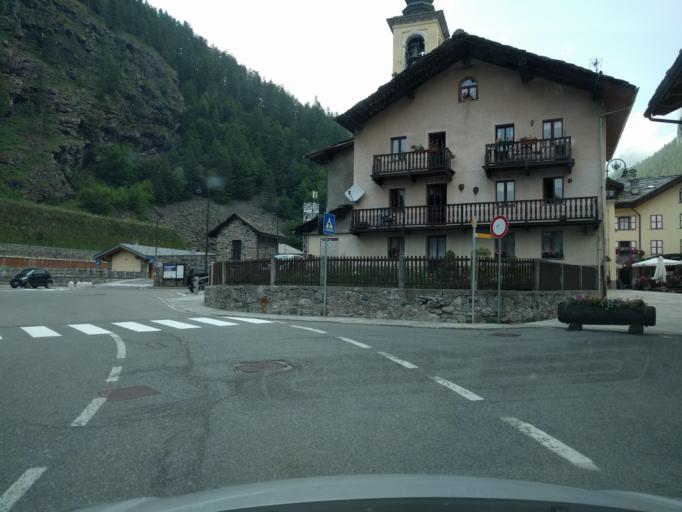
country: IT
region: Aosta Valley
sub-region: Valle d'Aosta
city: Gressoney-La-Trinite
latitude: 45.8269
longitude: 7.8228
